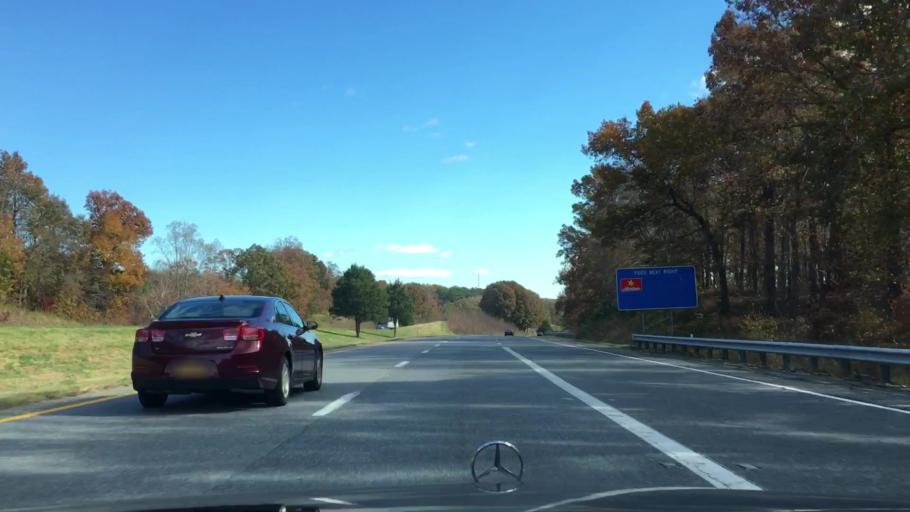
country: US
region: Virginia
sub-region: Campbell County
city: Altavista
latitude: 37.1391
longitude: -79.2655
